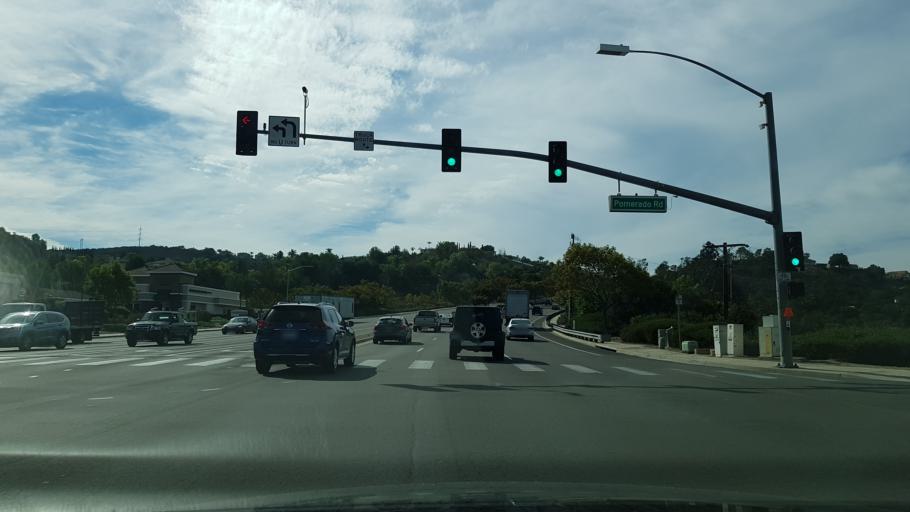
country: US
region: California
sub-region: San Diego County
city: Poway
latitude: 32.9352
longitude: -117.0603
